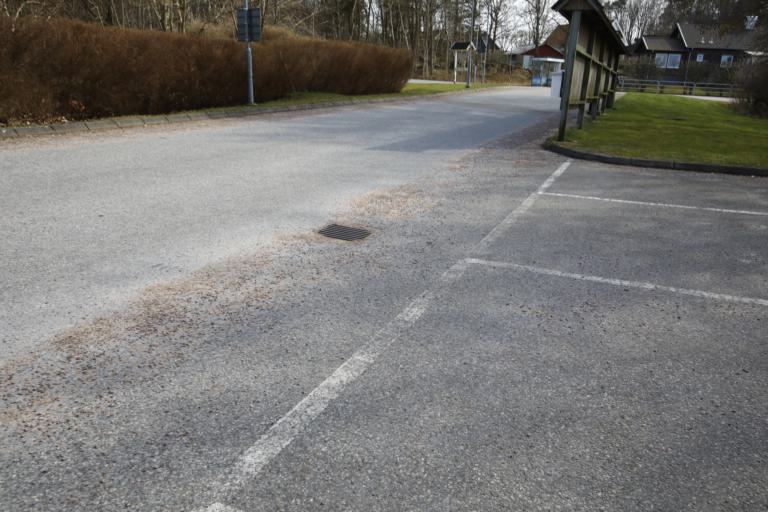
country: SE
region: Halland
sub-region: Varbergs Kommun
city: Varberg
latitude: 57.1388
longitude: 12.2835
